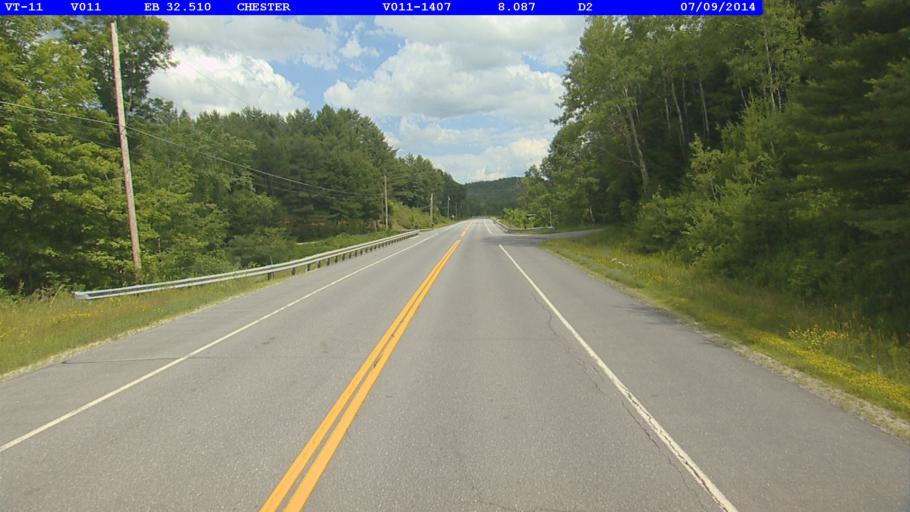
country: US
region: Vermont
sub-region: Windsor County
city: Chester
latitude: 43.2813
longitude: -72.5526
